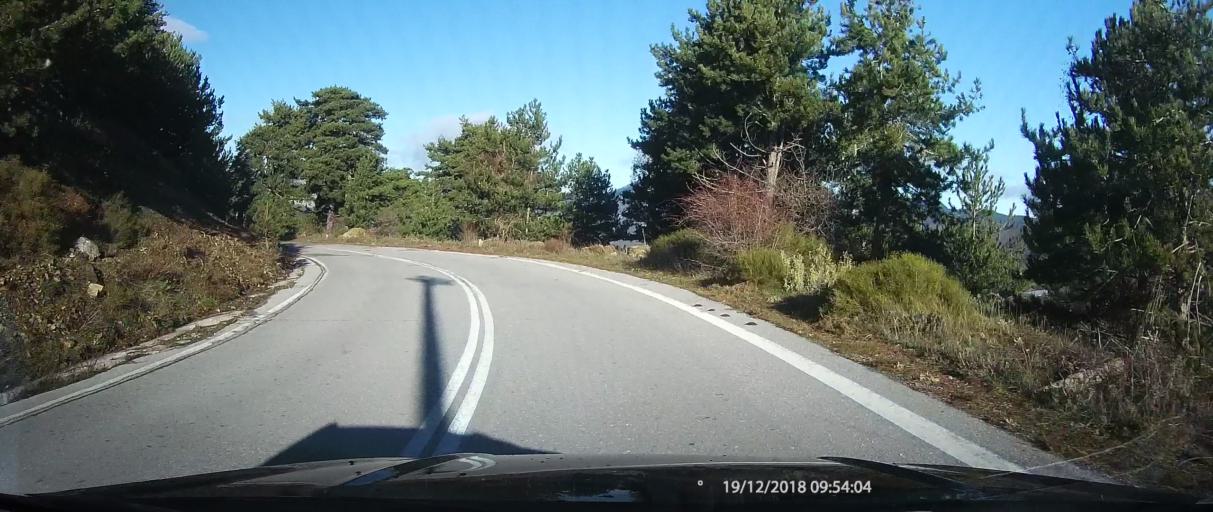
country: GR
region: Peloponnese
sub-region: Nomos Messinias
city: Paralia Vergas
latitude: 37.0783
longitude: 22.2503
